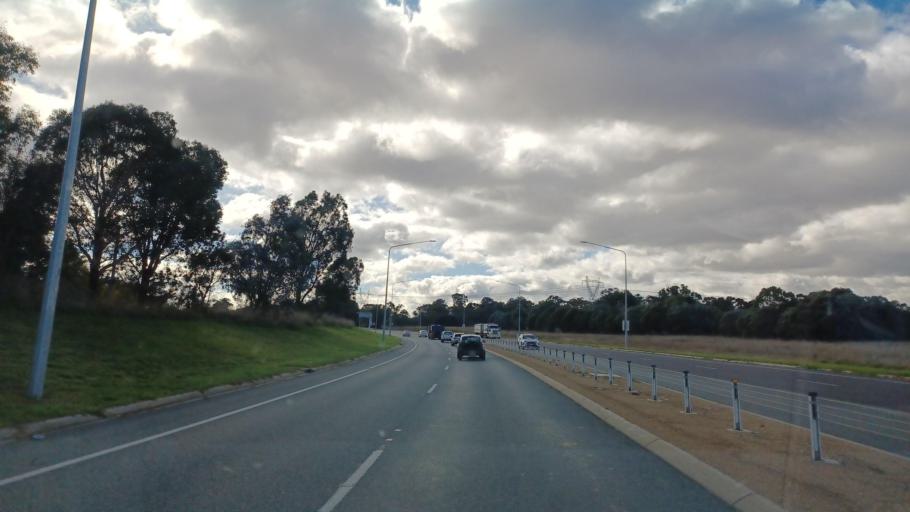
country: AU
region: Australian Capital Territory
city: Kaleen
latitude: -35.2232
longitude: 149.1277
